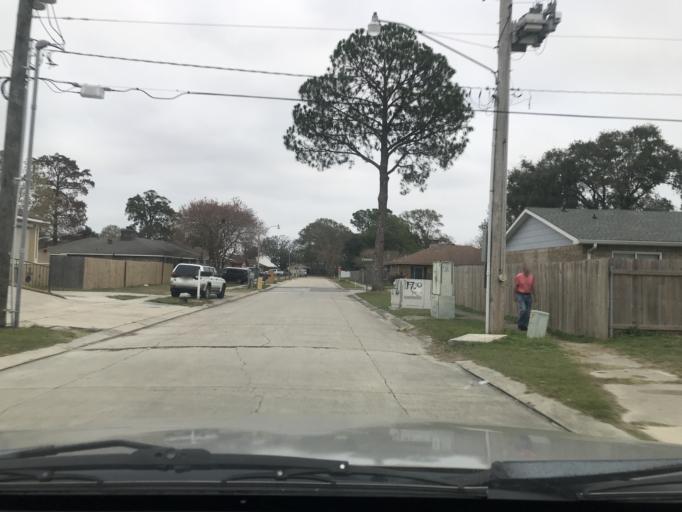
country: US
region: Louisiana
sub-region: Jefferson Parish
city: Woodmere
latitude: 29.8621
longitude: -90.0816
